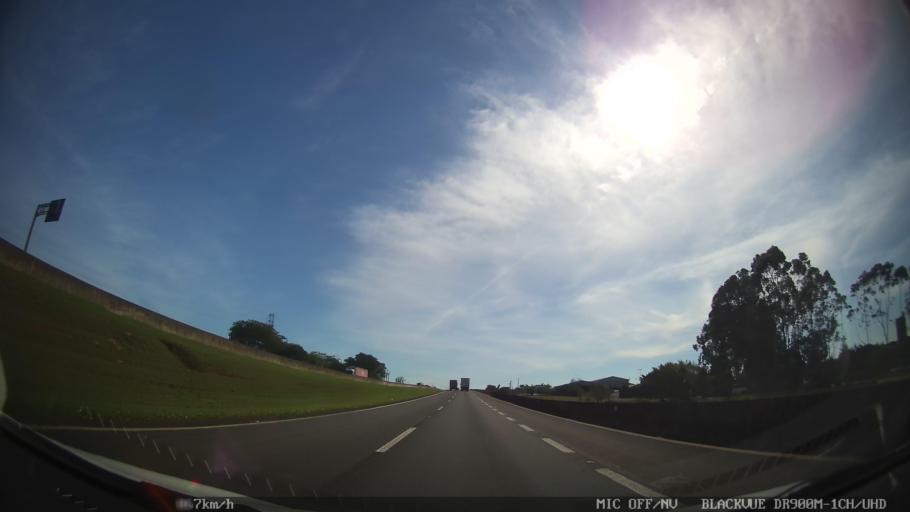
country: BR
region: Sao Paulo
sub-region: Leme
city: Leme
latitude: -22.1870
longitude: -47.3980
